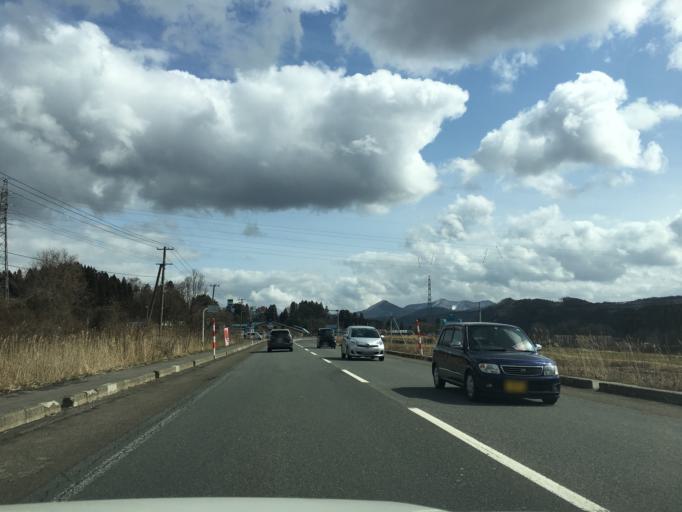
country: JP
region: Akita
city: Odate
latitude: 40.2289
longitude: 140.5964
